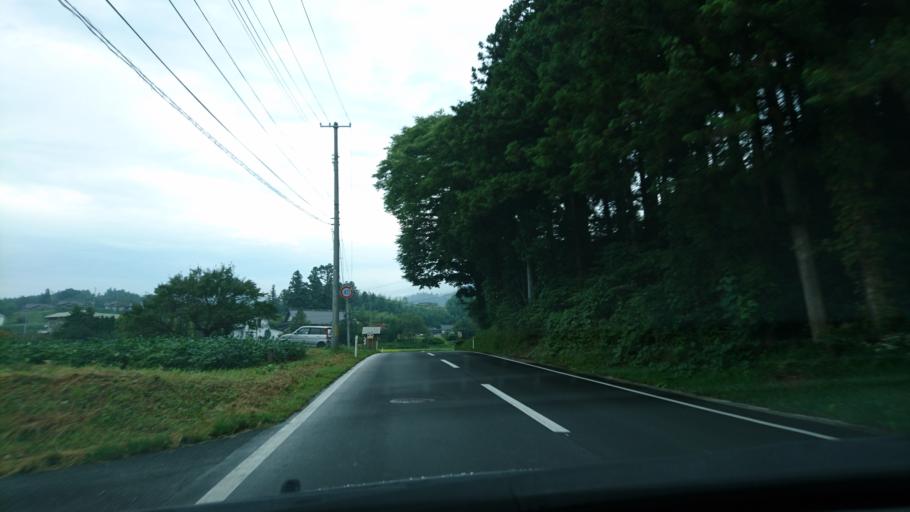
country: JP
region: Iwate
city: Ichinoseki
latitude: 38.9478
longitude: 141.2534
